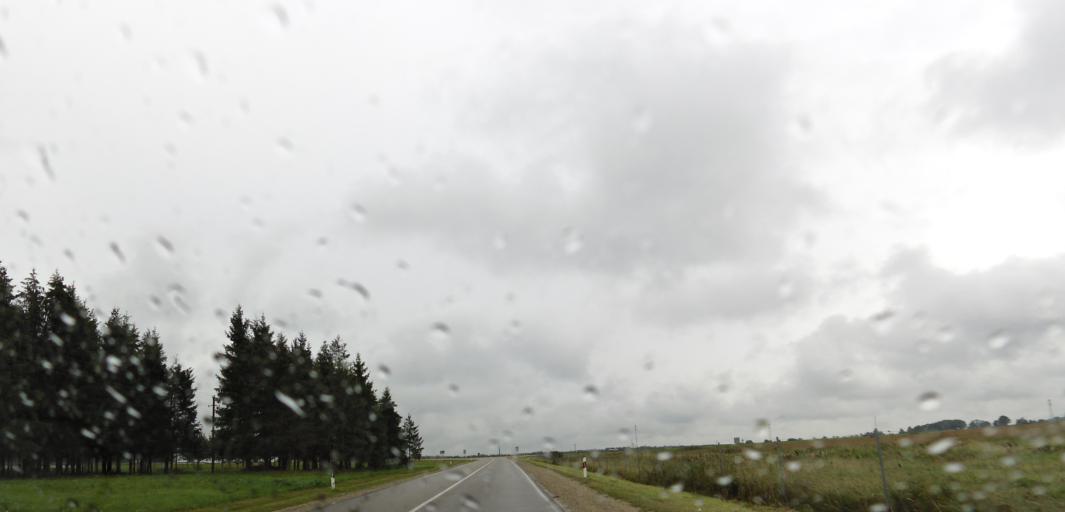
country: LT
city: Sirvintos
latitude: 55.0242
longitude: 24.9024
